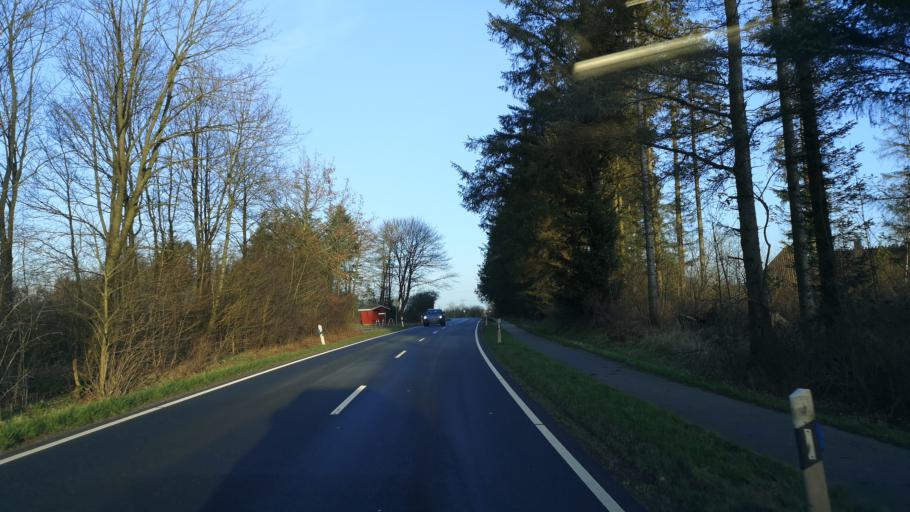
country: DE
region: Schleswig-Holstein
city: Sieverstedt
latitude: 54.6787
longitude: 9.4868
